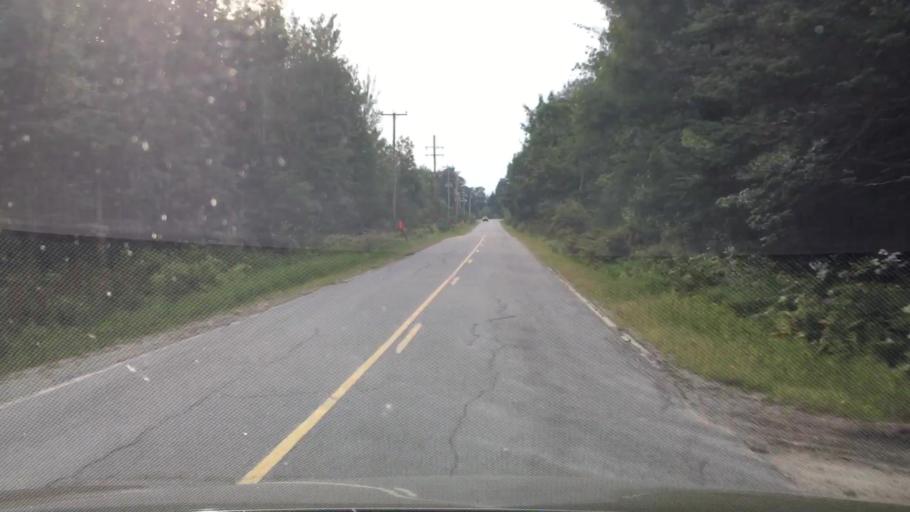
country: US
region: Maine
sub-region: Hancock County
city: Penobscot
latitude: 44.4737
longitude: -68.7746
